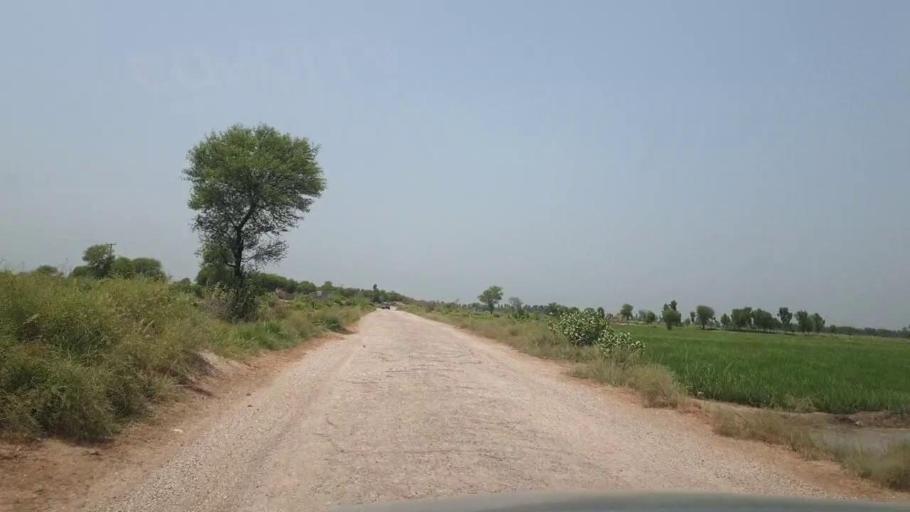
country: PK
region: Sindh
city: Garhi Yasin
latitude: 27.8829
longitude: 68.4417
